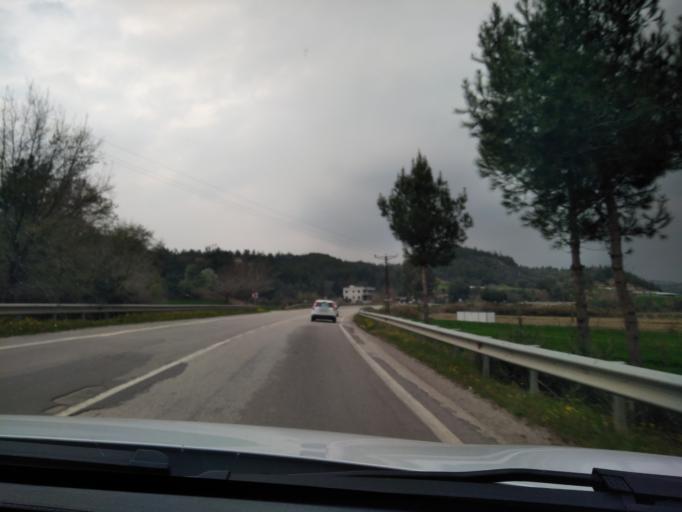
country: TR
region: Mersin
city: Yenice
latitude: 37.0958
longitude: 35.1117
